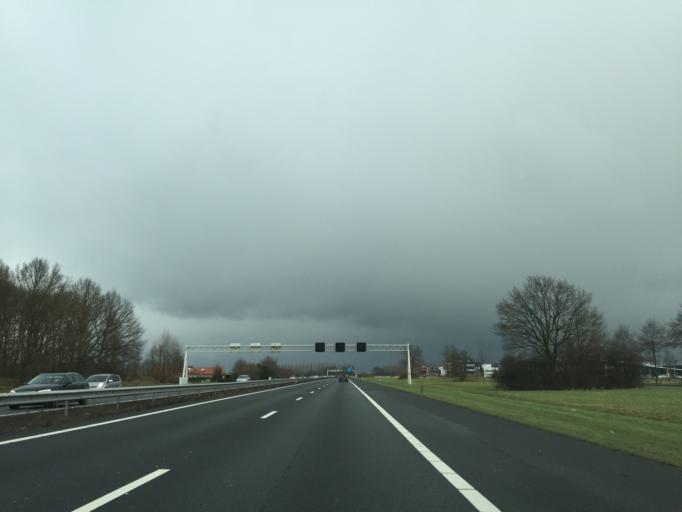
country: NL
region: Gelderland
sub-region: Gemeente Nijkerk
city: Nijkerk
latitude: 52.2265
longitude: 5.4561
